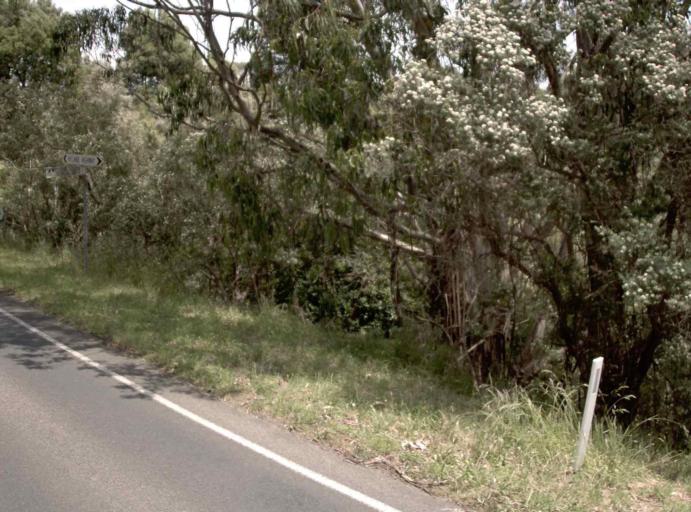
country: AU
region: Victoria
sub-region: Latrobe
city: Traralgon
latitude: -38.3430
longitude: 146.7243
